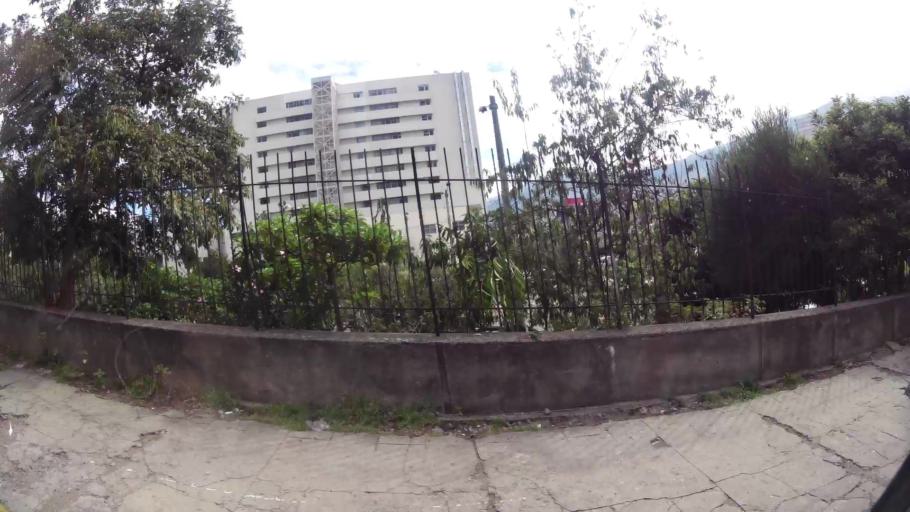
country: EC
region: Pichincha
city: Quito
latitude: -0.2142
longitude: -78.4973
